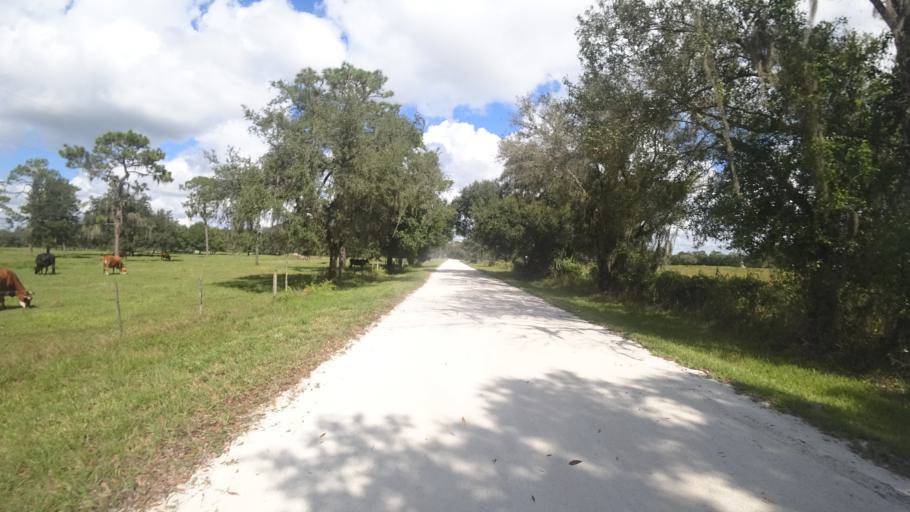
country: US
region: Florida
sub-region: Sarasota County
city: Lake Sarasota
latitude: 27.3838
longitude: -82.2193
